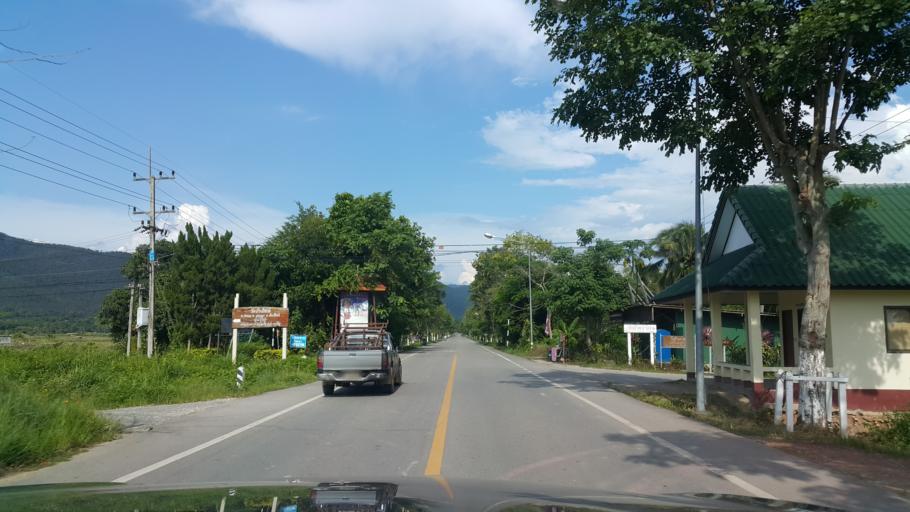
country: TH
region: Chiang Mai
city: Mae Taeng
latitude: 19.1437
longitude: 99.0255
